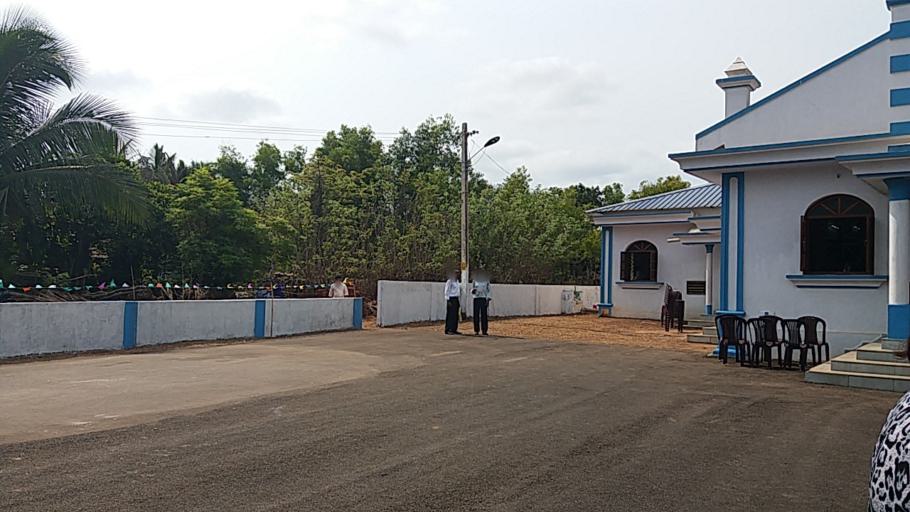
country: IN
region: Goa
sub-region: South Goa
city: Cuncolim
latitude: 15.1873
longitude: 74.0359
